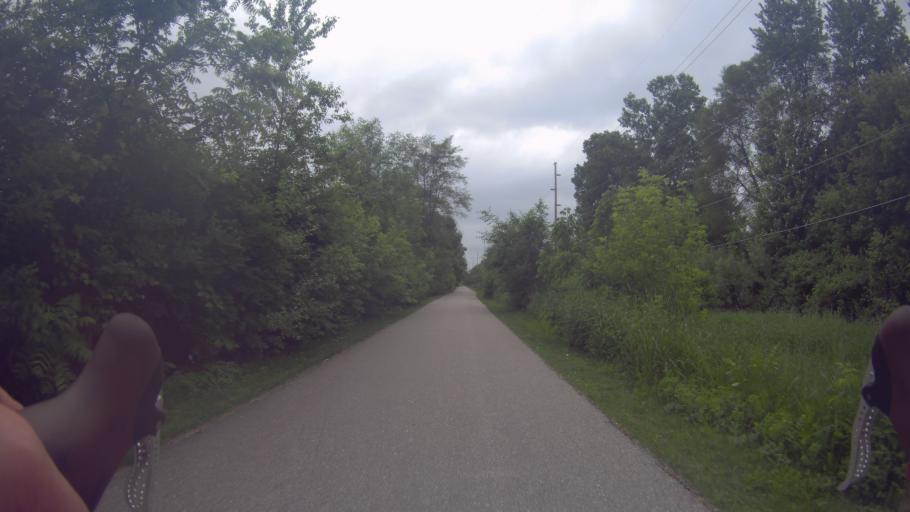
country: US
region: Wisconsin
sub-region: Dane County
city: Shorewood Hills
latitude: 43.0245
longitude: -89.4560
